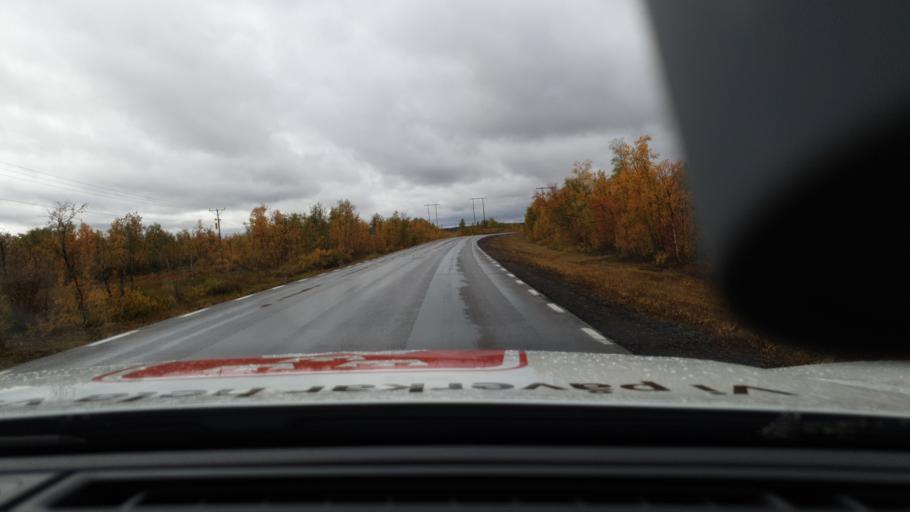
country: SE
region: Norrbotten
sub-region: Kiruna Kommun
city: Kiruna
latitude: 67.7799
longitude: 20.2239
